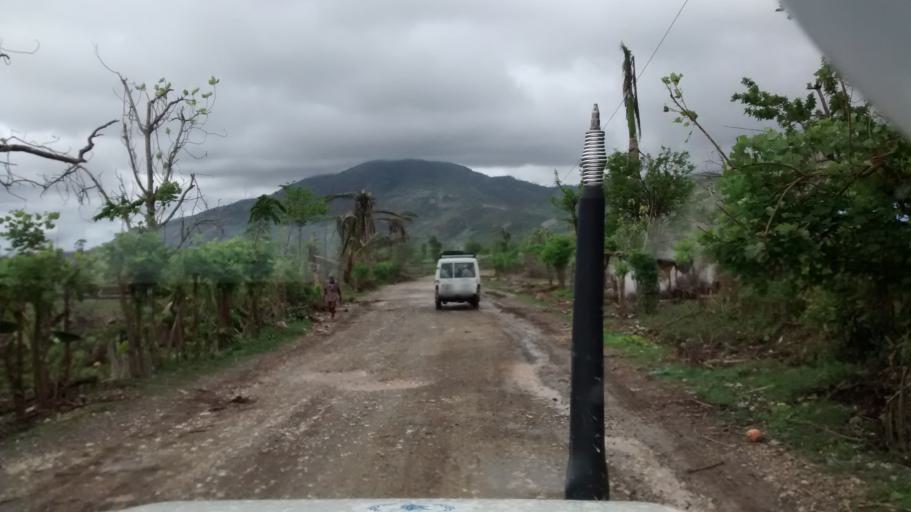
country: HT
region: Grandans
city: Moron
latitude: 18.5960
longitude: -74.1836
